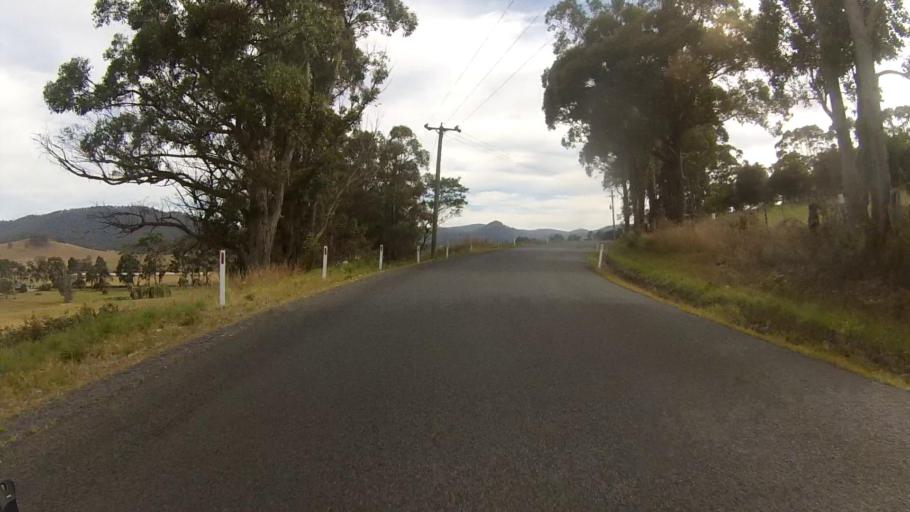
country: AU
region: Tasmania
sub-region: Sorell
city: Sorell
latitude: -42.7965
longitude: 147.7941
